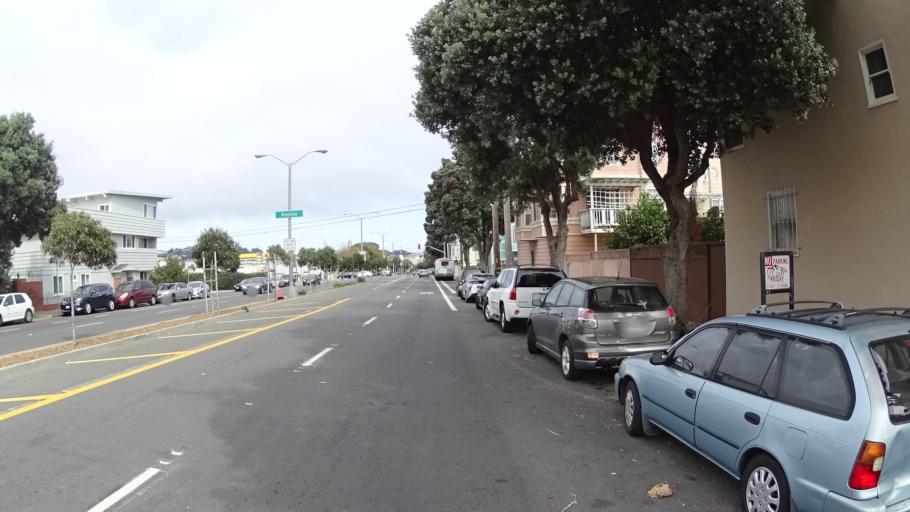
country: US
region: California
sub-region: San Mateo County
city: Daly City
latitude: 37.7170
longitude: -122.4433
